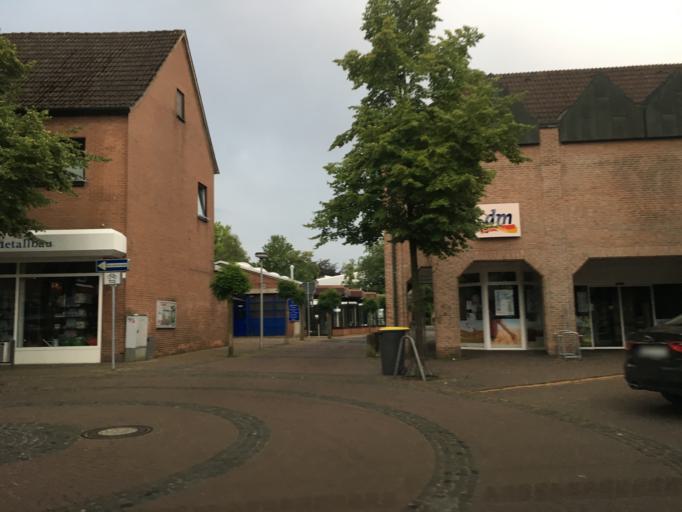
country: DE
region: North Rhine-Westphalia
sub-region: Regierungsbezirk Munster
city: Senden
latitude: 51.8562
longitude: 7.4861
